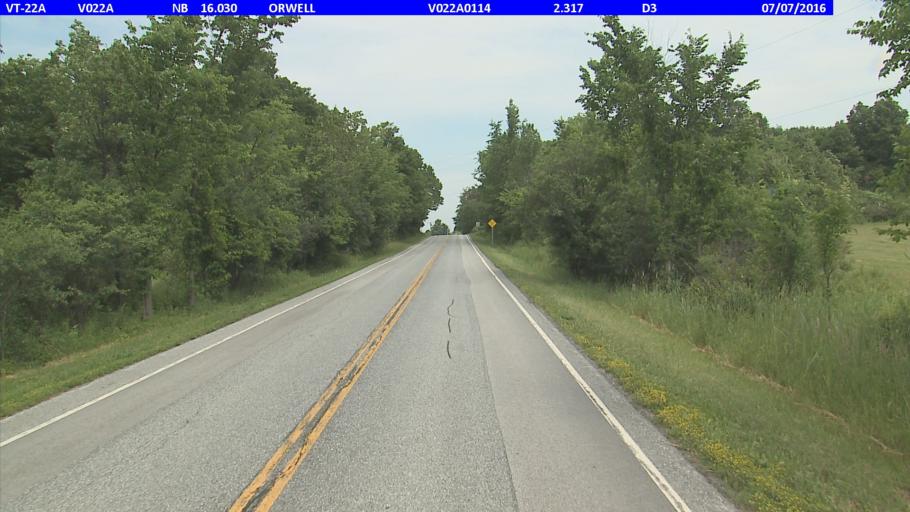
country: US
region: New York
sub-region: Essex County
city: Ticonderoga
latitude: 43.7904
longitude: -73.3067
